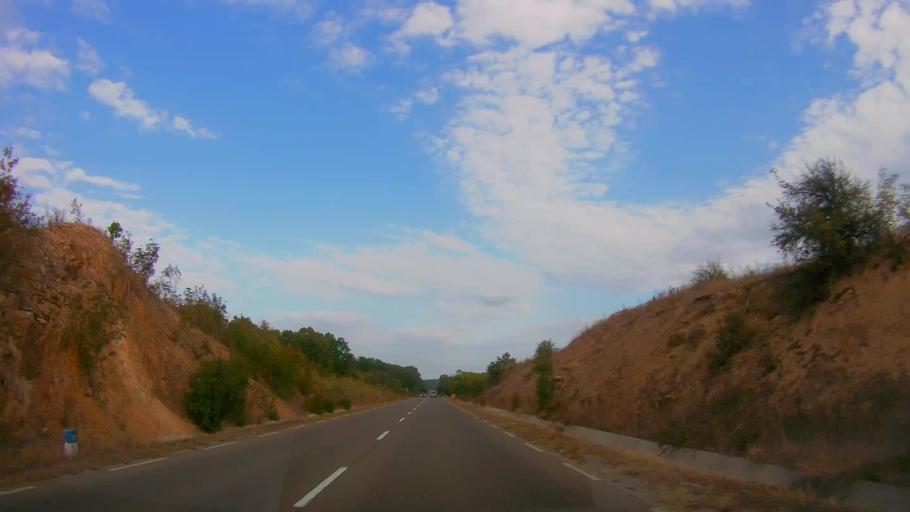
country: BG
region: Burgas
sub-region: Obshtina Sozopol
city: Sozopol
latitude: 42.3498
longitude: 27.7116
